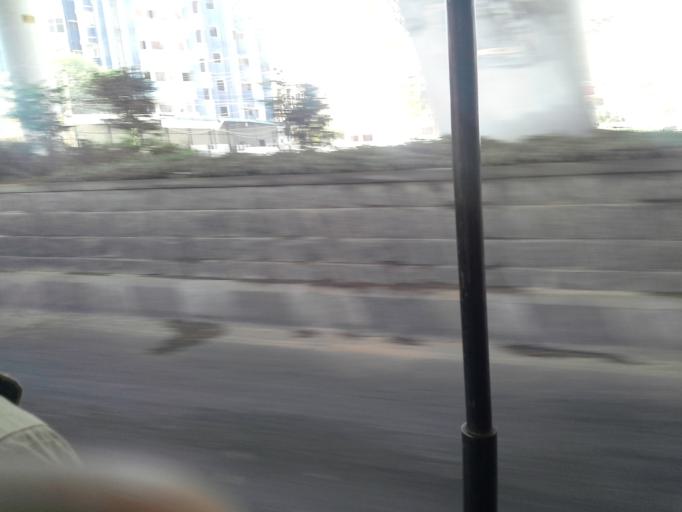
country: IN
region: Telangana
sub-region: Hyderabad
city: Hyderabad
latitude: 17.3471
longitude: 78.4162
